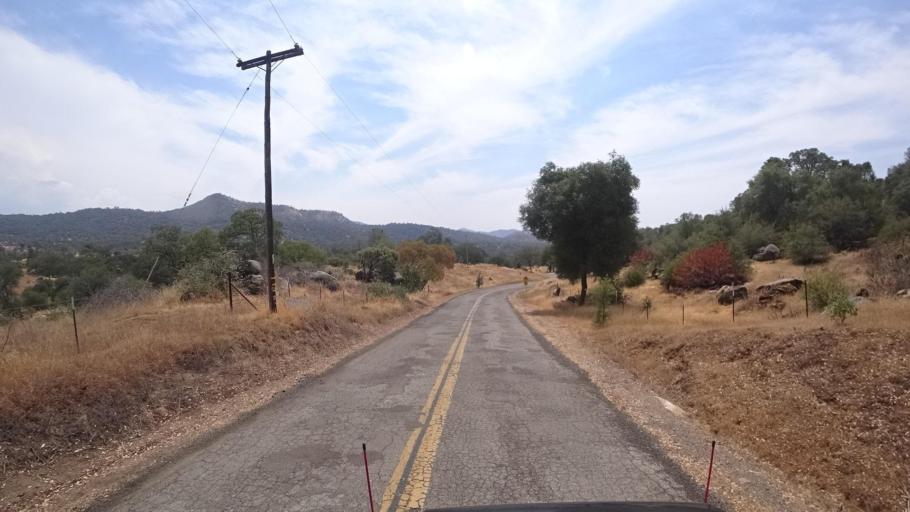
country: US
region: California
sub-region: Madera County
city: Ahwahnee
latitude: 37.3979
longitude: -119.8454
